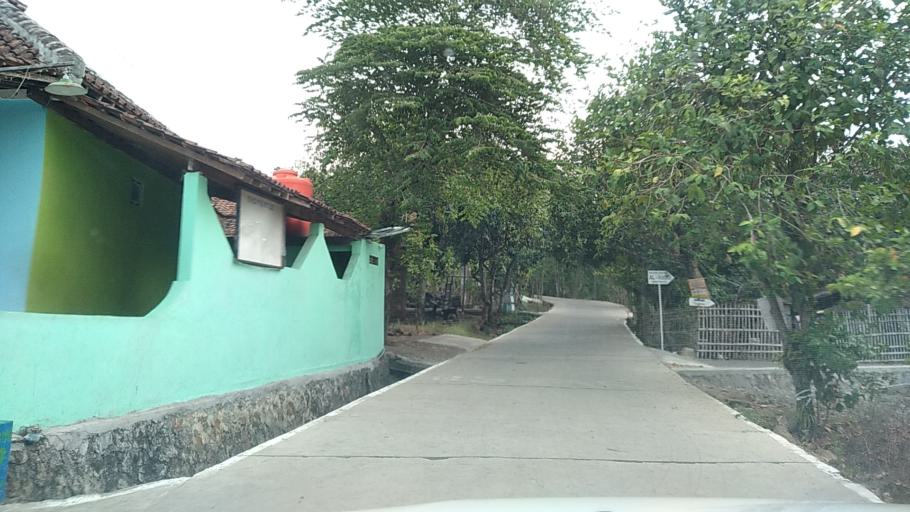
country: ID
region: Central Java
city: Semarang
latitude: -6.9933
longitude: 110.3073
